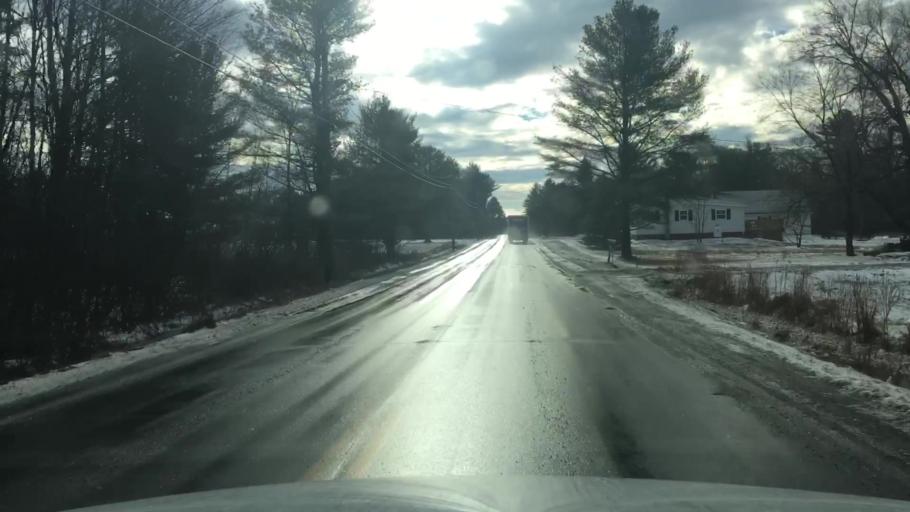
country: US
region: Maine
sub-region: Penobscot County
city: Brewer
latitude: 44.7483
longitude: -68.7671
